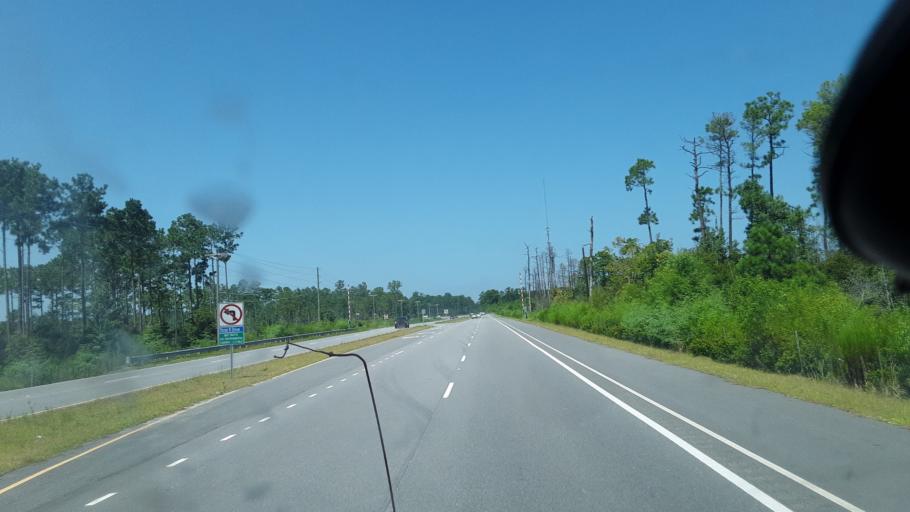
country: US
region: South Carolina
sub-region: Horry County
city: Forestbrook
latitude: 33.8134
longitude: -78.9008
